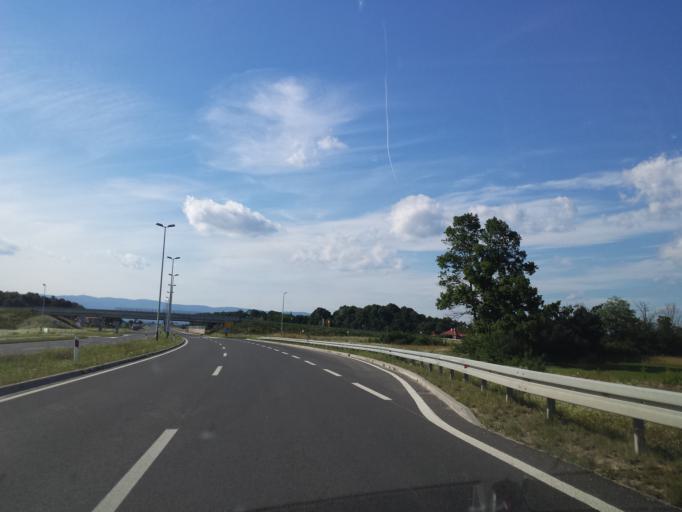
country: HR
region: Zagrebacka
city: Micevec
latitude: 45.7479
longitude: 16.1065
